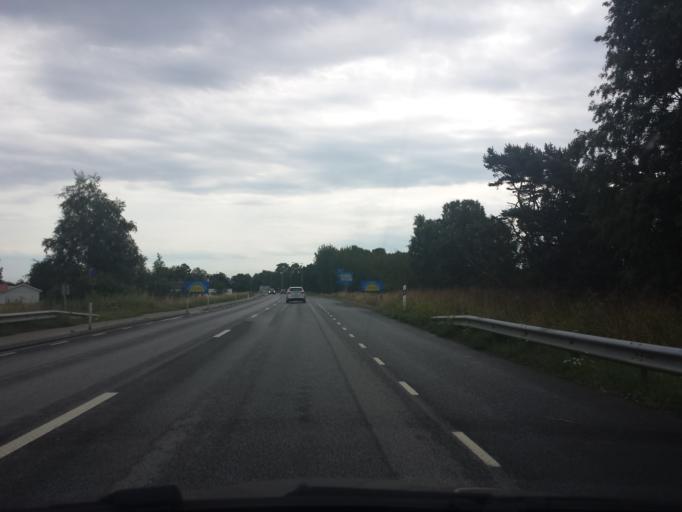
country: SE
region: Skane
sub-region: Ystads Kommun
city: Kopingebro
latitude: 55.4355
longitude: 13.9216
